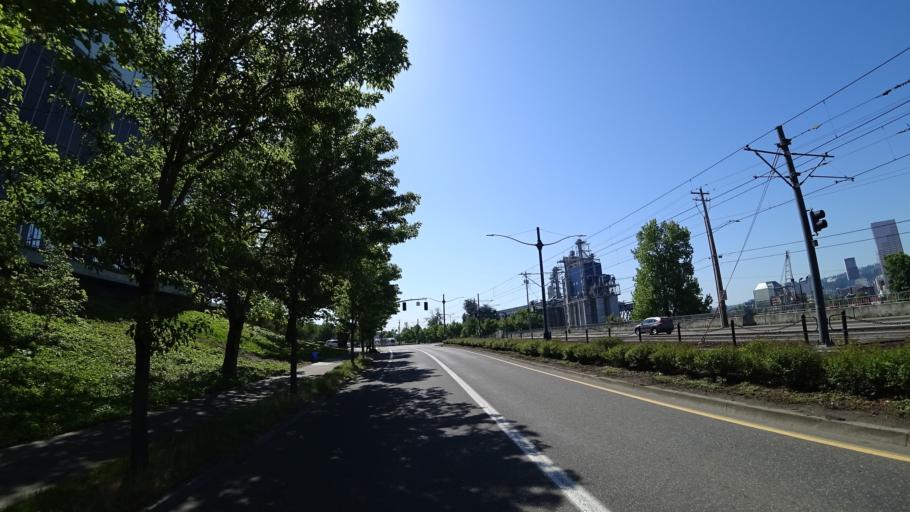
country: US
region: Oregon
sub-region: Multnomah County
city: Portland
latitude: 45.5316
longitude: -122.6701
